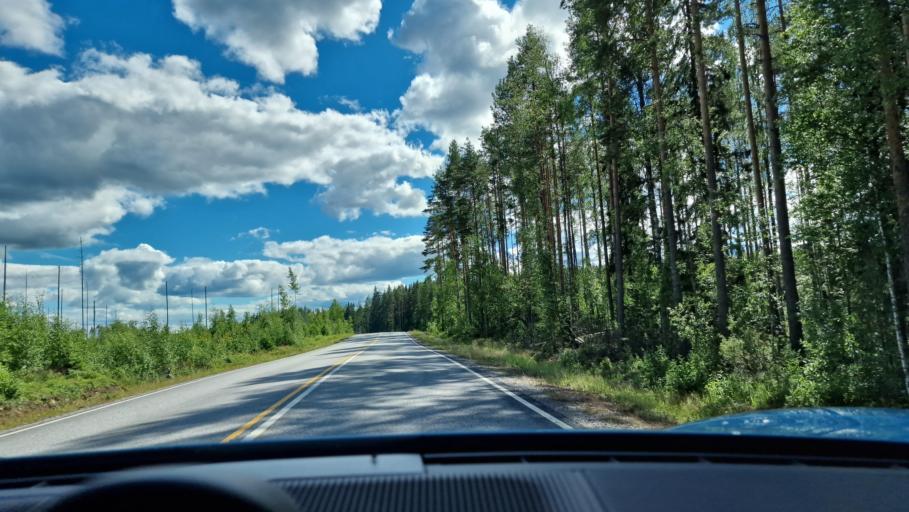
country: FI
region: Central Finland
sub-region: Saarijaervi-Viitasaari
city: Pylkoenmaeki
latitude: 62.6505
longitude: 24.5723
